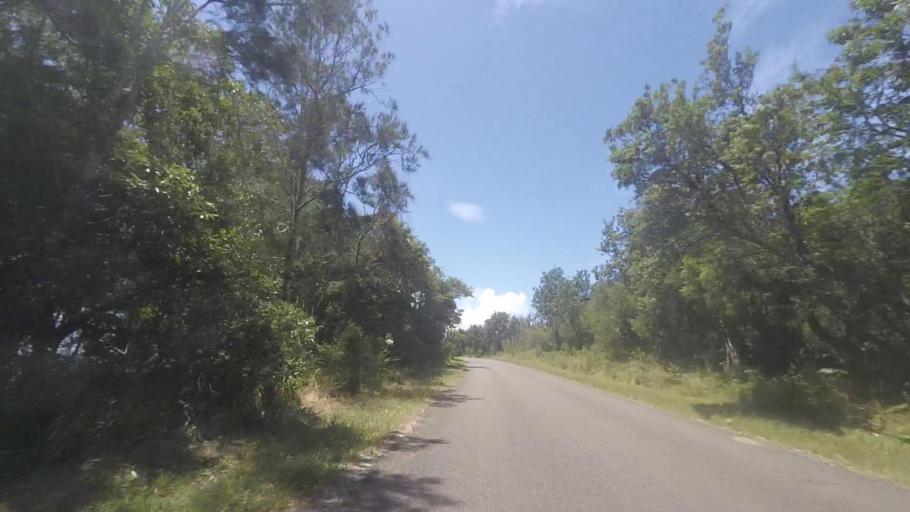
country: AU
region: New South Wales
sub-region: Great Lakes
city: Bulahdelah
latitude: -32.5377
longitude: 152.3183
